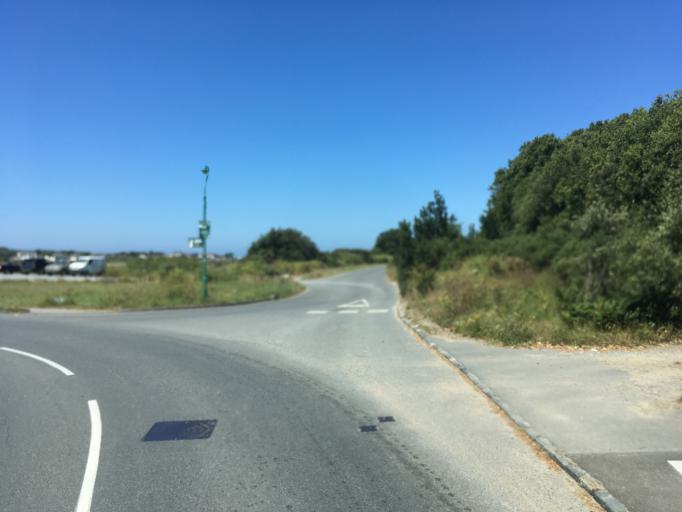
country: GG
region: St Peter Port
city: Saint Peter Port
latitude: 49.4927
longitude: -2.5406
